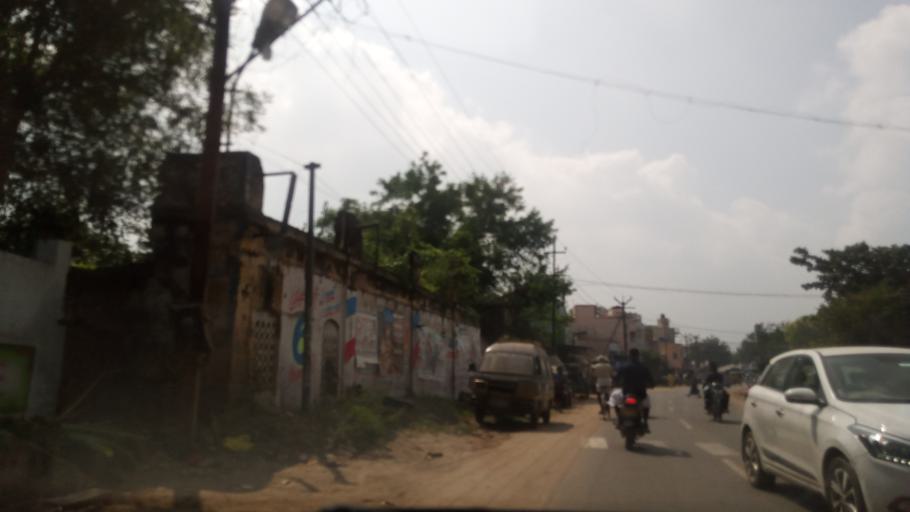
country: IN
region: Tamil Nadu
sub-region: Vellore
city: Arakkonam
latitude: 13.0779
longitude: 79.6717
